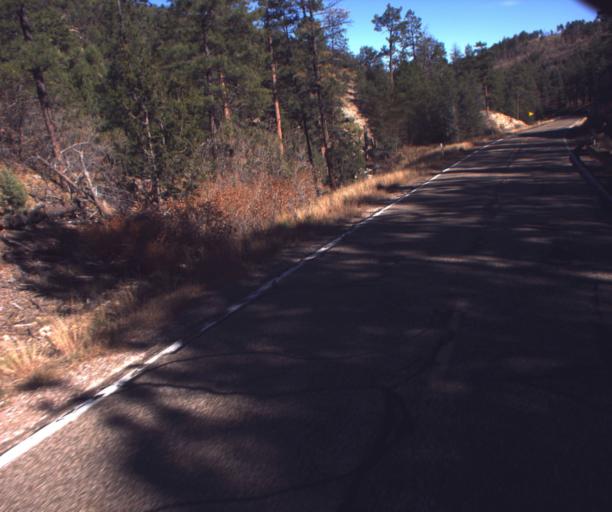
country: US
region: Arizona
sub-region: Coconino County
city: Fredonia
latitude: 36.7317
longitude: -112.1563
